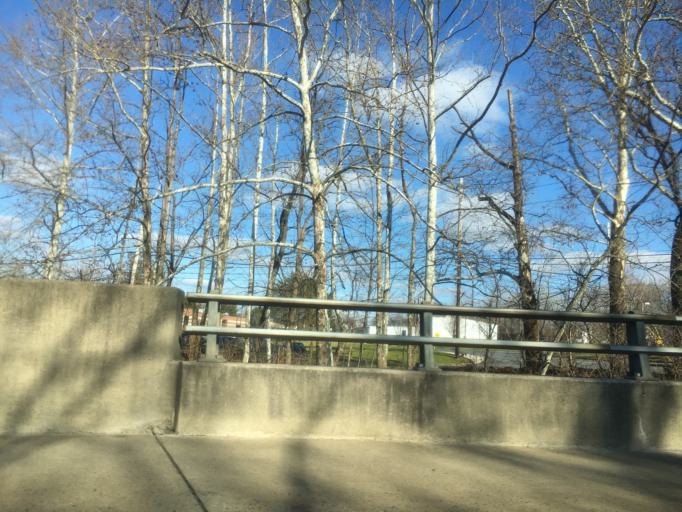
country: US
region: Pennsylvania
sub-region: Northampton County
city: Northampton
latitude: 40.6793
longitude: -75.4891
